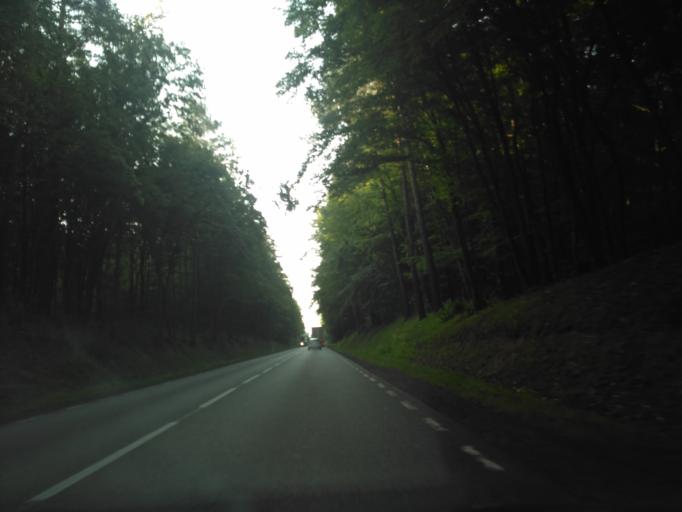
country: PL
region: Lublin Voivodeship
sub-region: Powiat krasnicki
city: Szastarka
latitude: 50.8517
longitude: 22.2880
